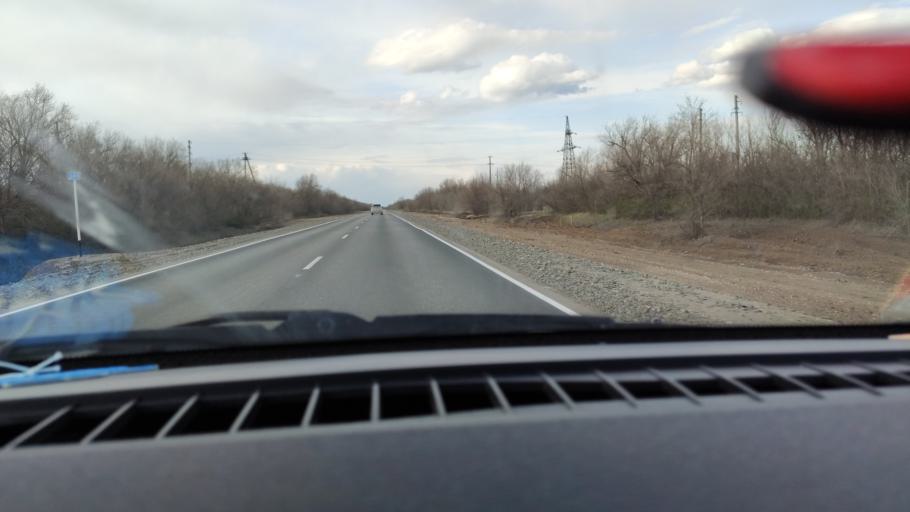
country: RU
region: Saratov
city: Krasnoarmeysk
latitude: 51.1366
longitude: 45.9600
